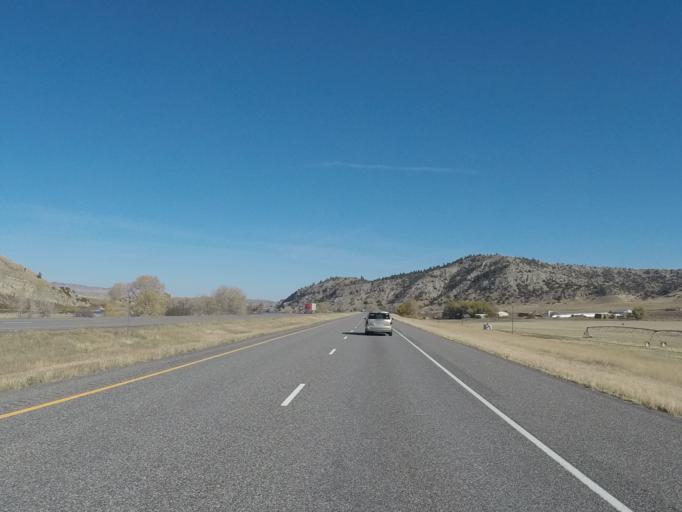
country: US
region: Montana
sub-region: Sweet Grass County
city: Big Timber
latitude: 45.7218
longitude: -110.2496
